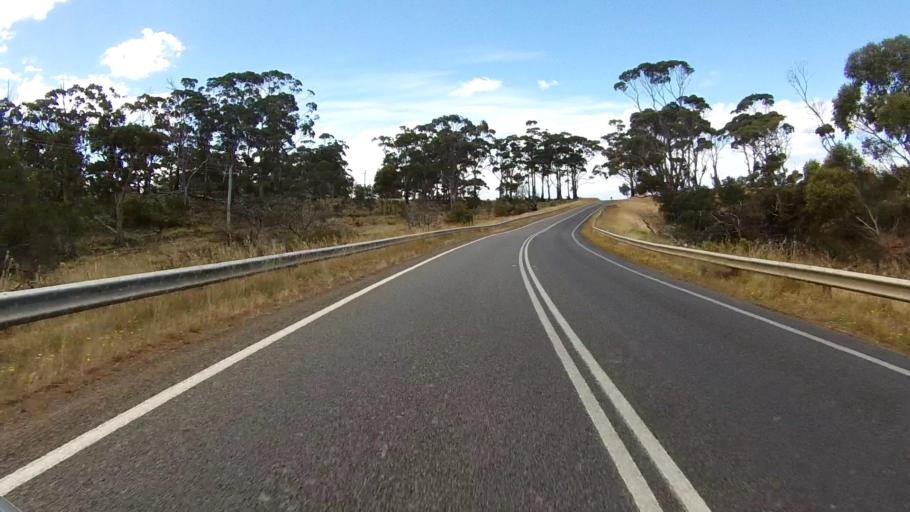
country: AU
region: Tasmania
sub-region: Sorell
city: Sorell
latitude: -42.2128
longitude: 148.0340
